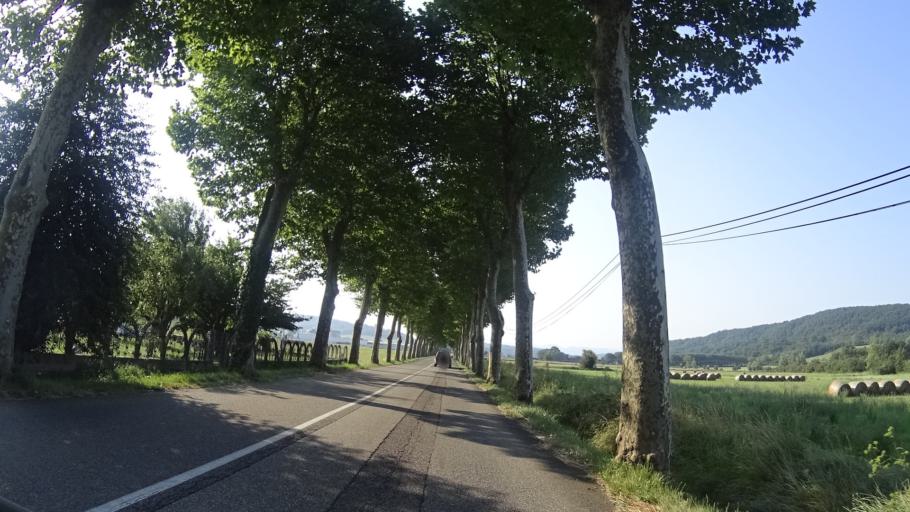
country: FR
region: Midi-Pyrenees
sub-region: Departement de l'Ariege
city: Mirepoix
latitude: 43.0520
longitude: 1.8879
